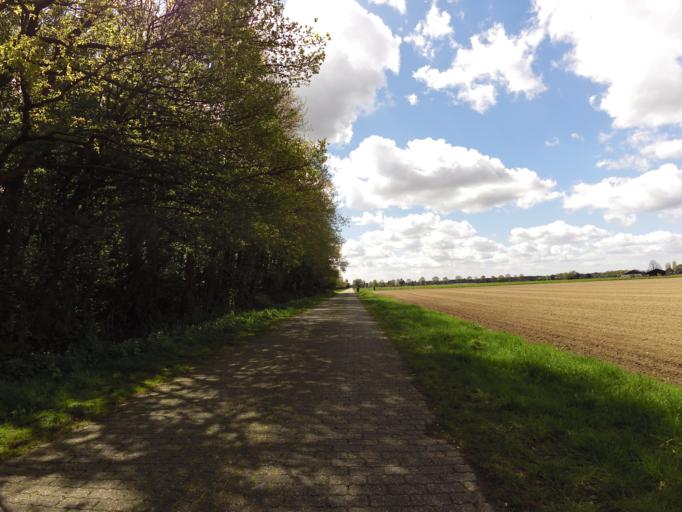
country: NL
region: Gelderland
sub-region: Gemeente Montferland
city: s-Heerenberg
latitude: 51.9367
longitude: 6.1922
